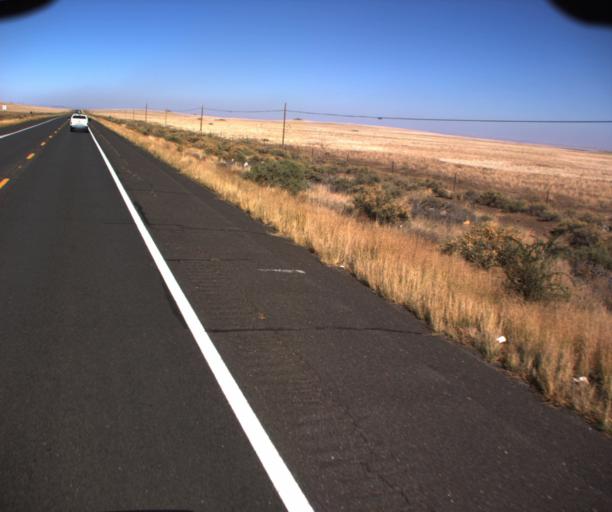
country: US
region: Arizona
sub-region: Coconino County
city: Flagstaff
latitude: 35.5933
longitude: -111.5272
